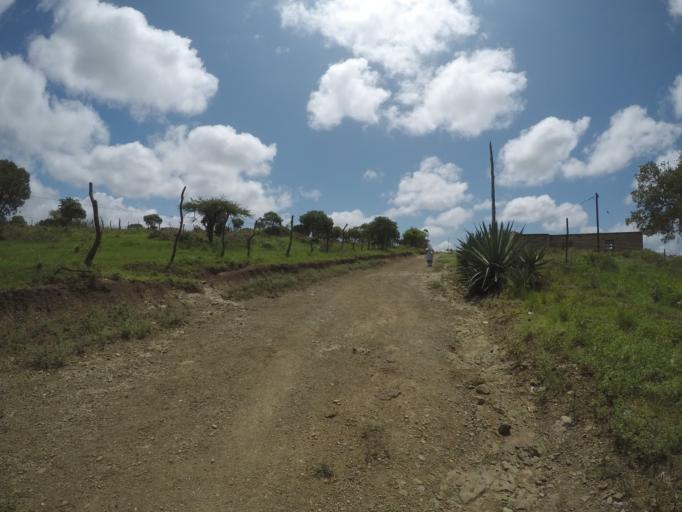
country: ZA
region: KwaZulu-Natal
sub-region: uThungulu District Municipality
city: Empangeni
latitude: -28.5782
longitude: 31.8382
